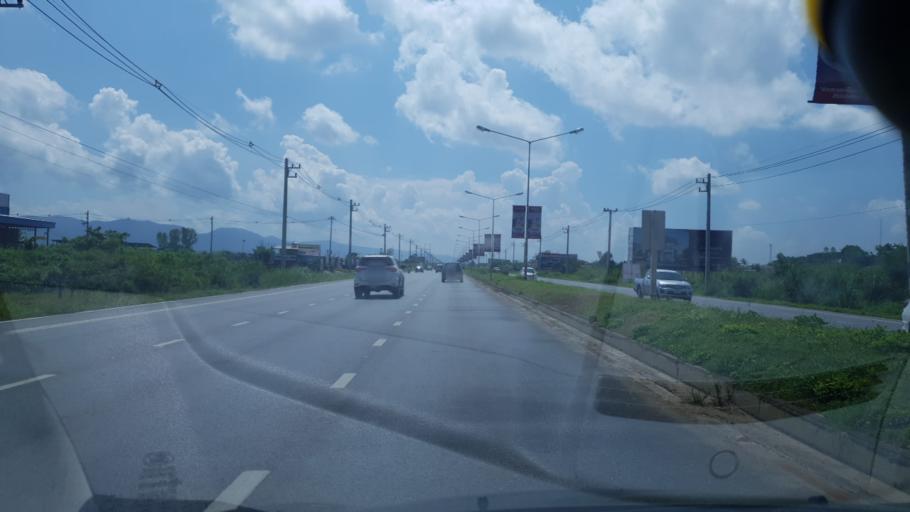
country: TH
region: Chiang Rai
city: Chiang Rai
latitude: 19.8854
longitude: 99.8525
